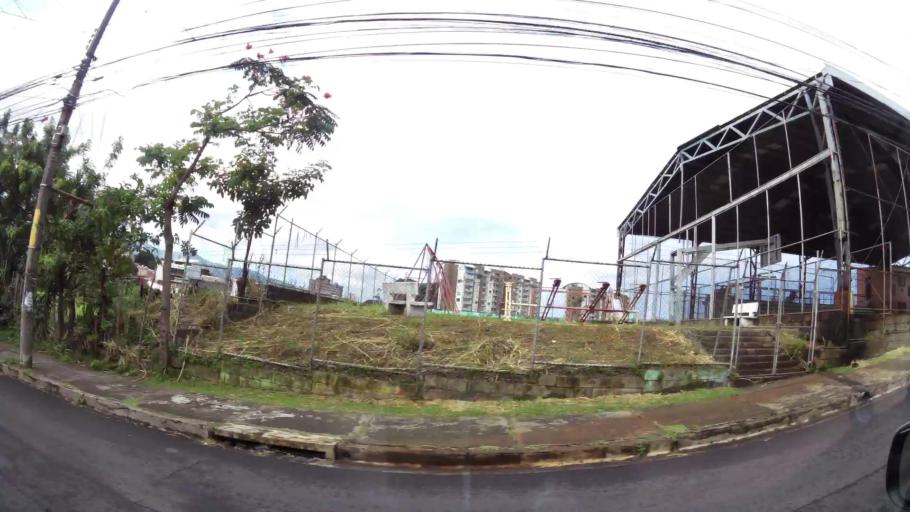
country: CR
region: San Jose
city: Colima
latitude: 9.9413
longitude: -84.0935
